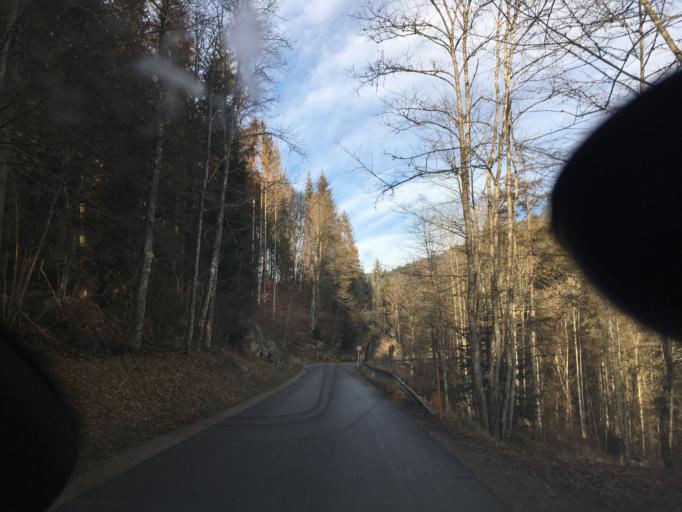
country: DE
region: Baden-Wuerttemberg
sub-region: Freiburg Region
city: Hausern
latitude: 47.7483
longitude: 8.1890
